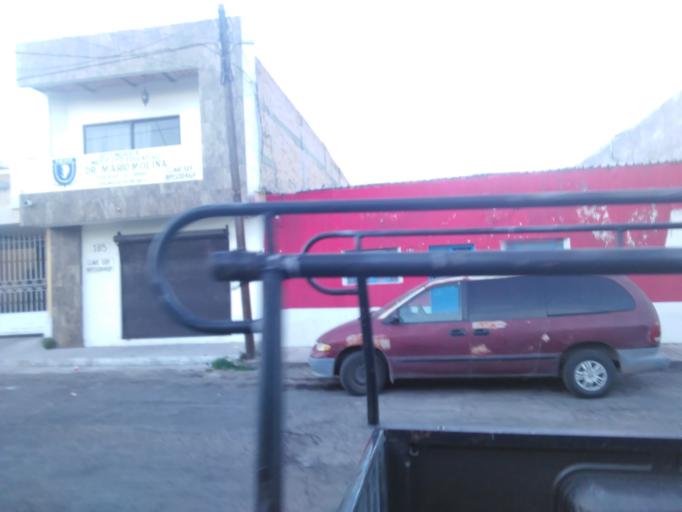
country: MX
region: Nayarit
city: Tepic
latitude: 21.4866
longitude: -104.8899
